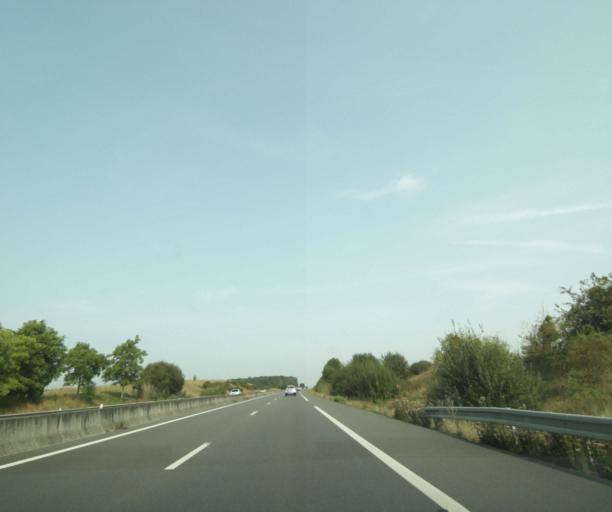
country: FR
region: Pays de la Loire
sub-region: Departement de la Sarthe
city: Champfleur
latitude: 48.3360
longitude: 0.1059
